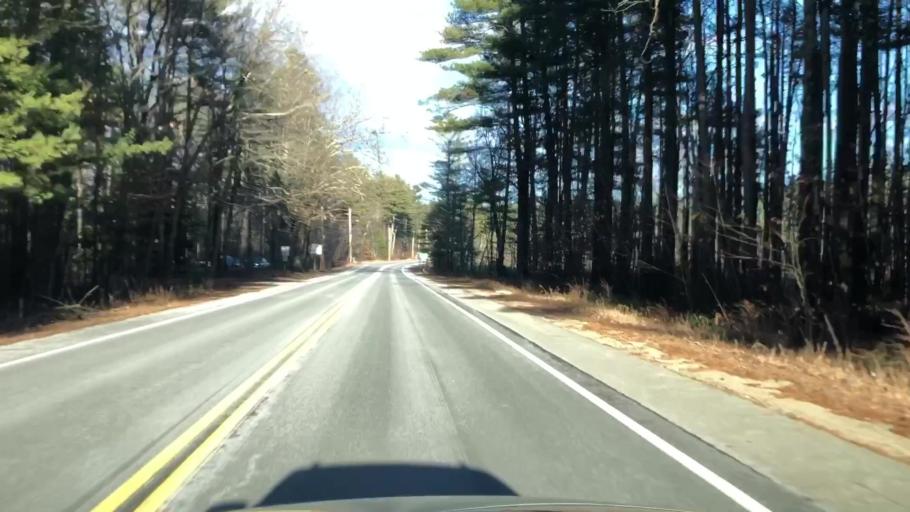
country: US
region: New Hampshire
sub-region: Hillsborough County
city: Brookline
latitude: 42.7046
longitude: -71.6735
